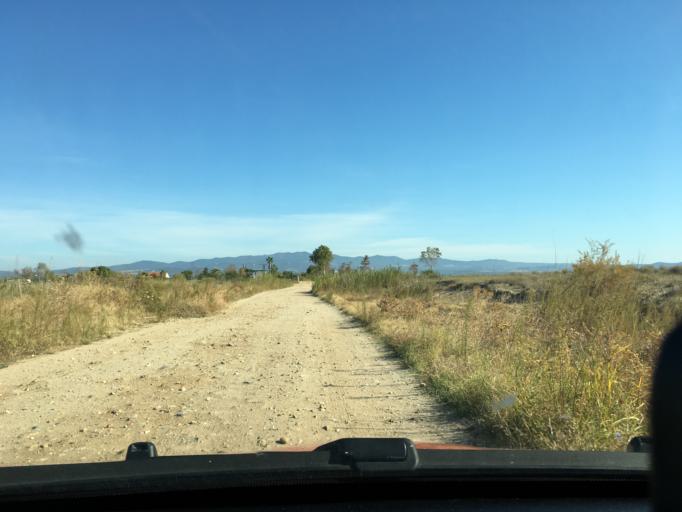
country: GR
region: Central Macedonia
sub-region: Nomos Chalkidikis
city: Nea Potidhaia
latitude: 40.2392
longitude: 23.3474
